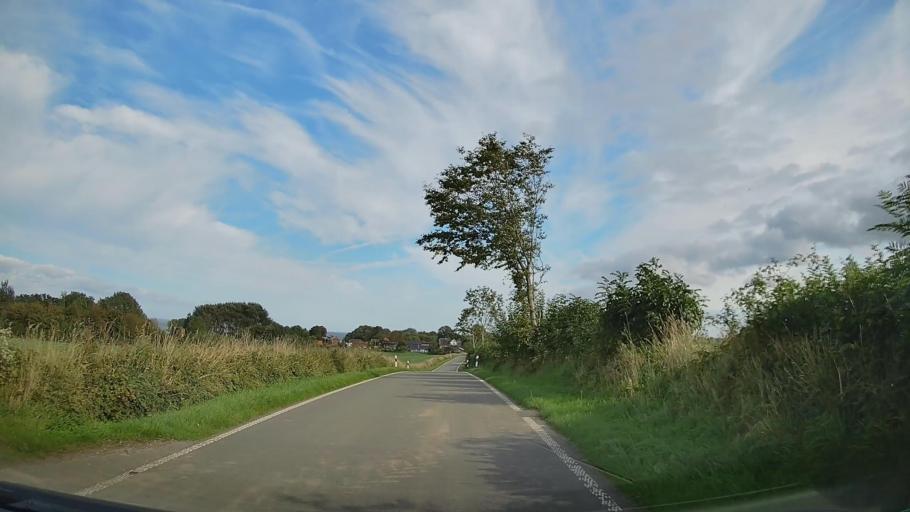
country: DE
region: Schleswig-Holstein
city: Steinbergkirche
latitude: 54.8009
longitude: 9.7485
